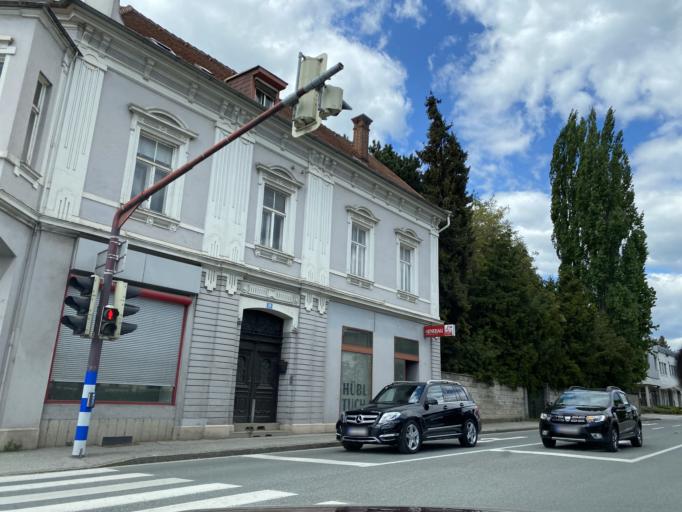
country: AT
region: Carinthia
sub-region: Politischer Bezirk Wolfsberg
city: Wolfsberg
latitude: 46.8405
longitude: 14.8404
